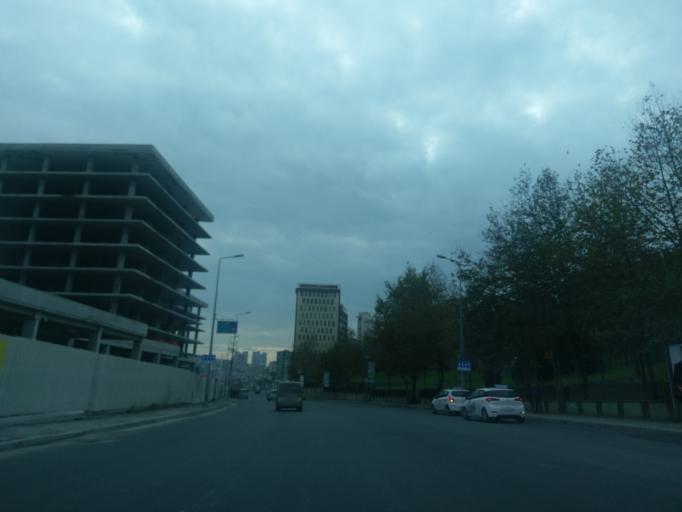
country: TR
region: Istanbul
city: Sisli
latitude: 41.0983
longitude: 28.9783
